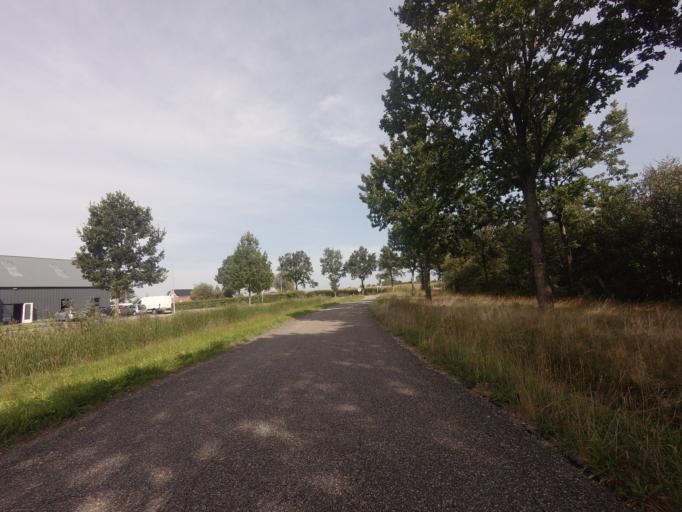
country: NL
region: Groningen
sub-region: Gemeente Leek
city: Leek
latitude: 53.1895
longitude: 6.3762
